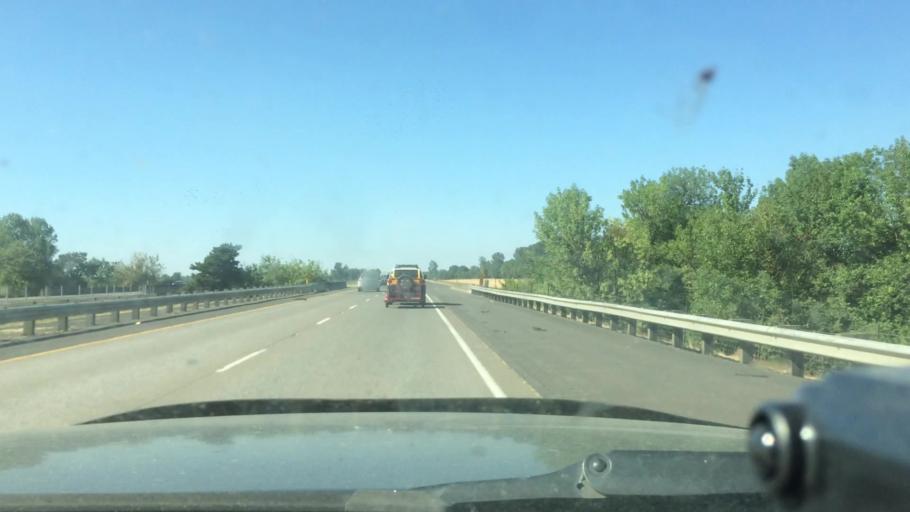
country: US
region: Oregon
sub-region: Linn County
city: Brownsville
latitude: 44.4430
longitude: -123.0613
